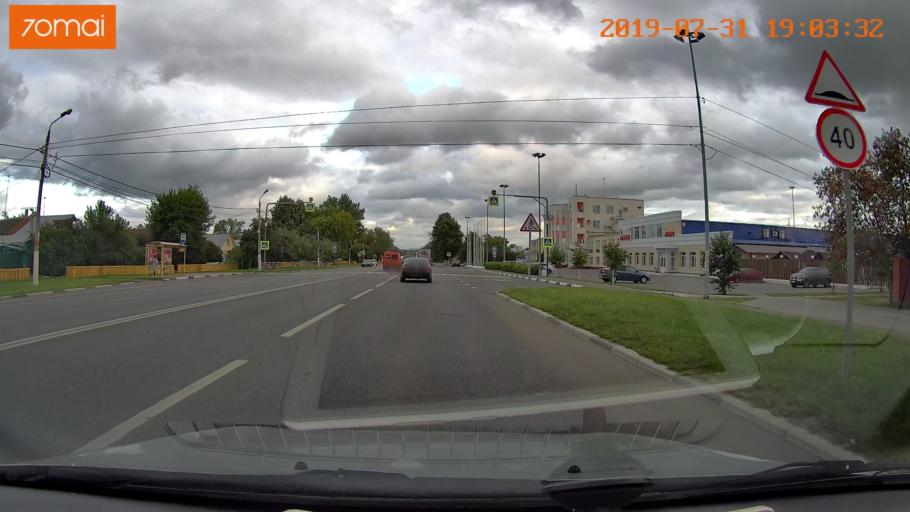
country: RU
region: Moskovskaya
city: Raduzhnyy
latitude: 55.1140
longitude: 38.7376
